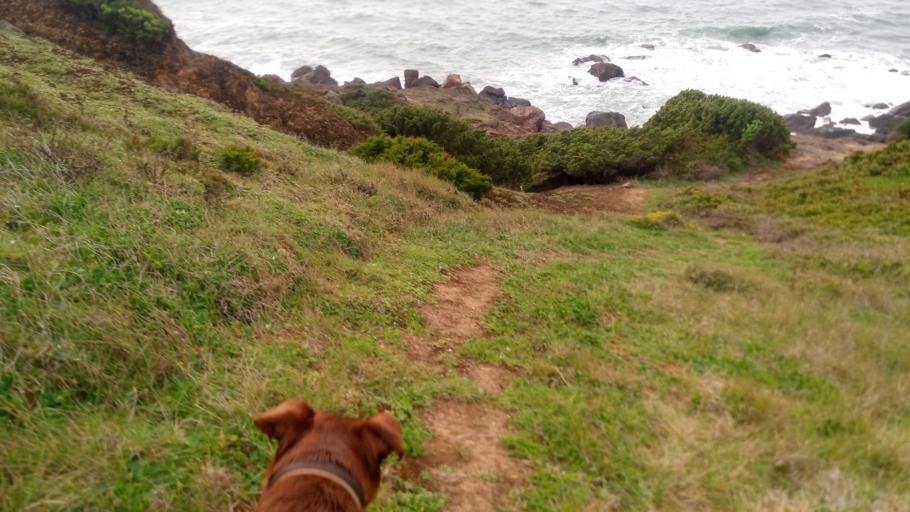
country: PT
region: Leiria
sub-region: Caldas da Rainha
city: Caldas da Rainha
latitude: 39.4882
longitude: -9.1814
